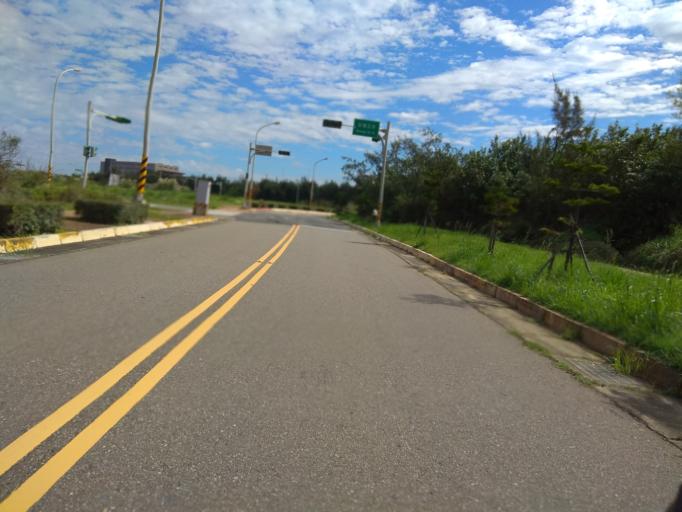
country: TW
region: Taiwan
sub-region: Hsinchu
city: Zhubei
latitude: 25.0446
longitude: 121.0830
